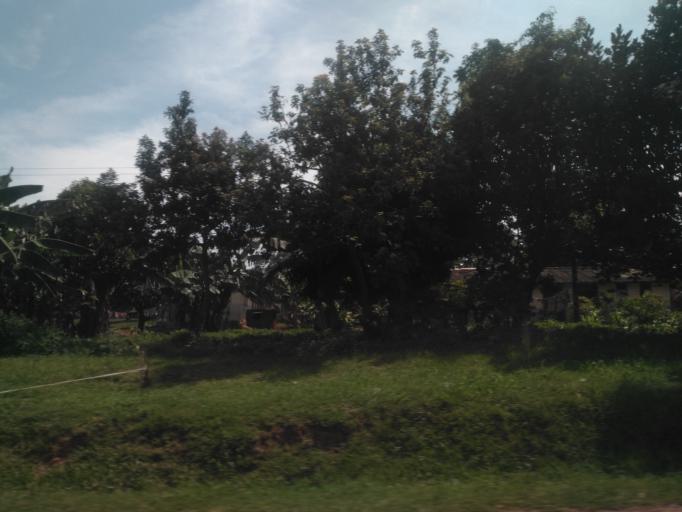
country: UG
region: Central Region
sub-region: Wakiso District
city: Entebbe
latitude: 0.0497
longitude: 32.4568
